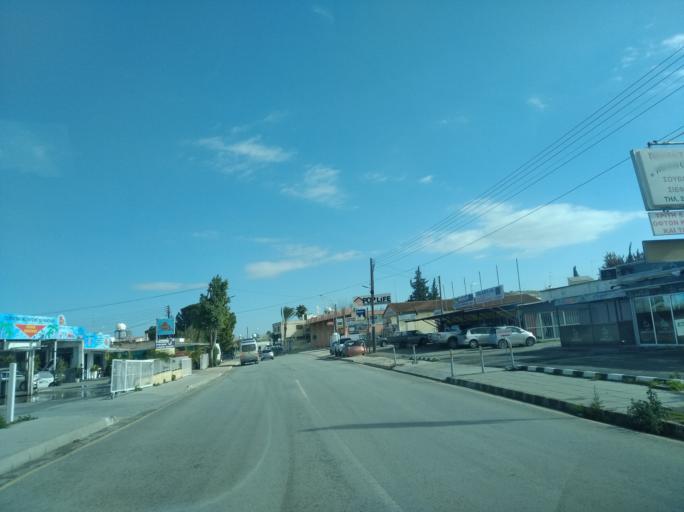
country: CY
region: Lefkosia
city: Dali
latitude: 35.0191
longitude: 33.4168
